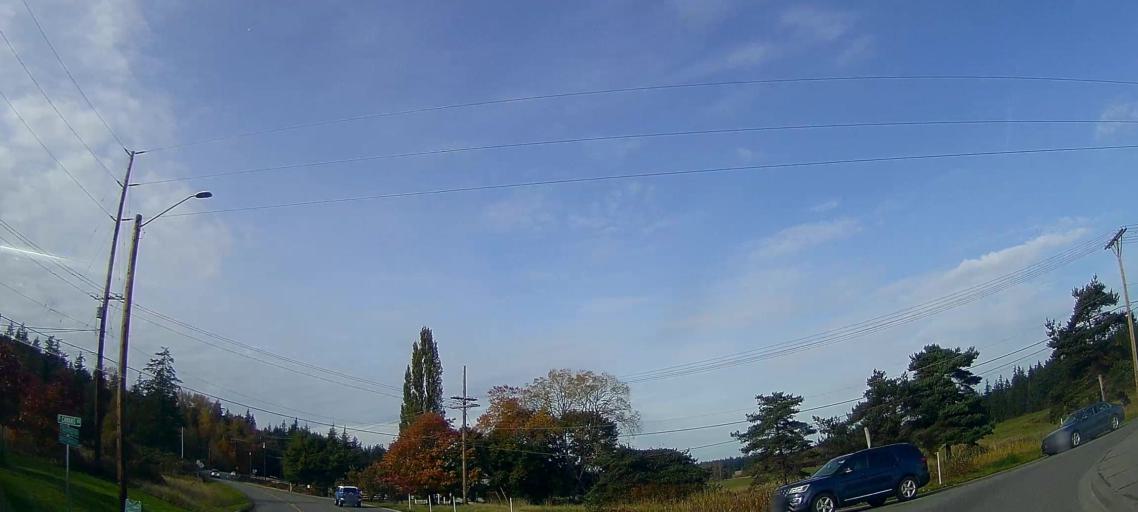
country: US
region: Washington
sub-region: Snohomish County
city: Stanwood
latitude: 48.2424
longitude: -122.4567
